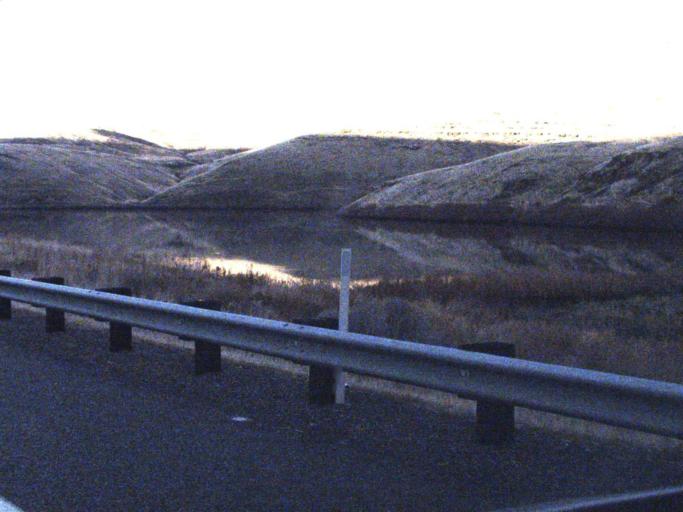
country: US
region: Washington
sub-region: Garfield County
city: Pomeroy
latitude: 46.6088
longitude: -117.7878
